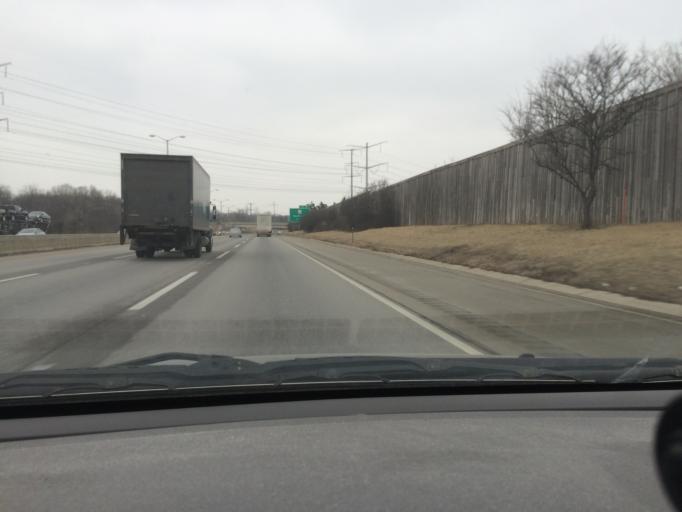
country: US
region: Illinois
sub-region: DuPage County
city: Lombard
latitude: 41.8851
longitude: -88.0349
